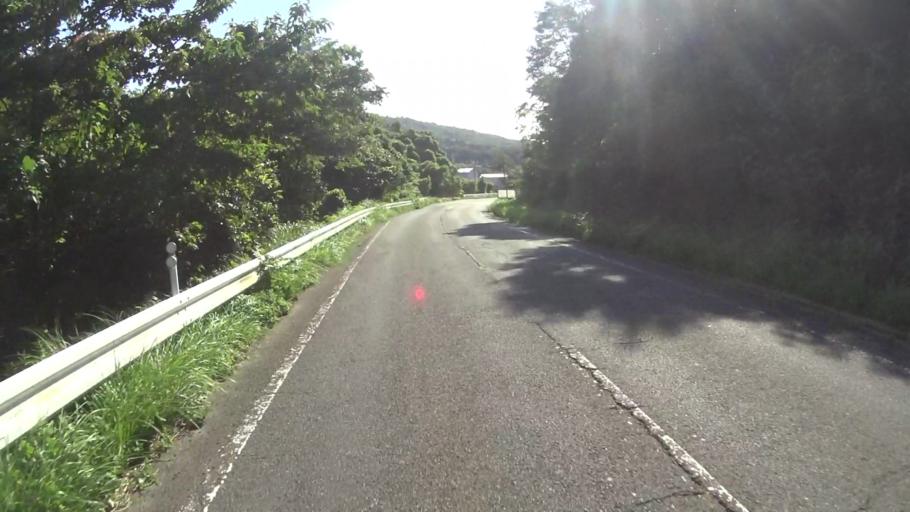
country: JP
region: Kyoto
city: Miyazu
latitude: 35.7026
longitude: 135.0682
